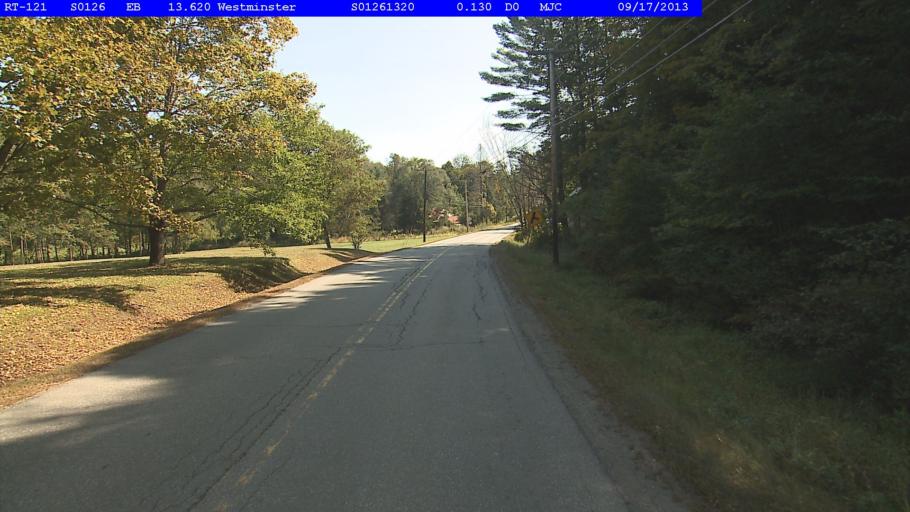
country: US
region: Vermont
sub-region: Windham County
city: Bellows Falls
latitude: 43.1250
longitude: -72.4750
